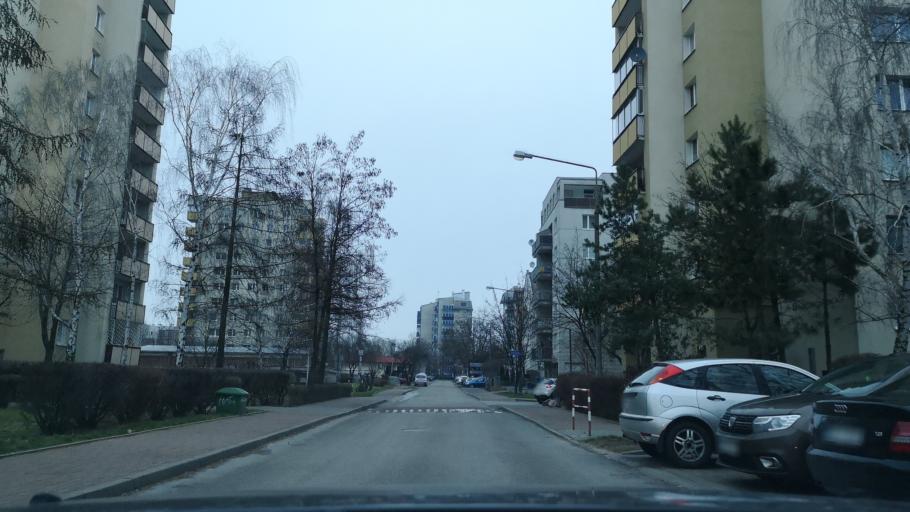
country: PL
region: Masovian Voivodeship
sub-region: Warszawa
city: Bemowo
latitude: 52.2419
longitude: 20.9182
